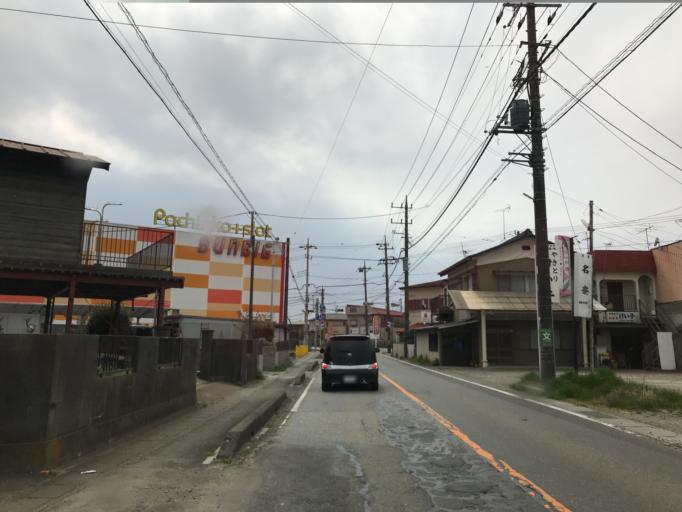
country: JP
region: Ibaraki
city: Ushiku
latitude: 35.9875
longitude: 140.0591
